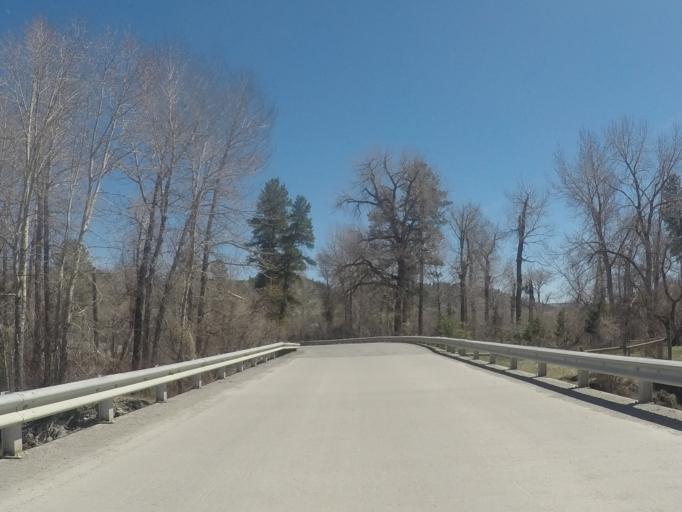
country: US
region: Montana
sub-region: Stillwater County
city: Columbus
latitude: 45.6235
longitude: -109.2887
